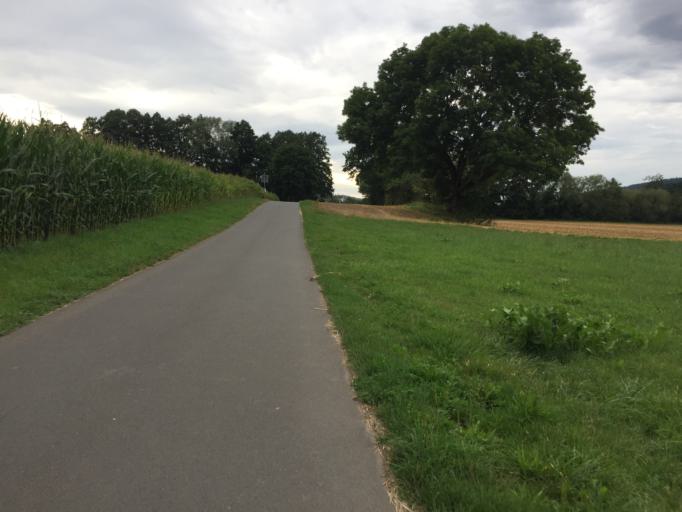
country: DE
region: Hesse
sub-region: Regierungsbezirk Kassel
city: Rotenburg an der Fulda
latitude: 50.9906
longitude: 9.7489
